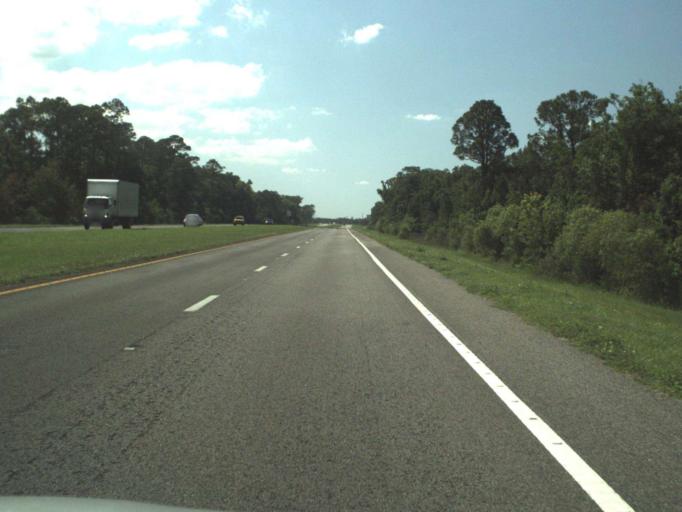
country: US
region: Florida
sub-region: Orange County
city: Christmas
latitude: 28.4572
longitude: -80.9846
